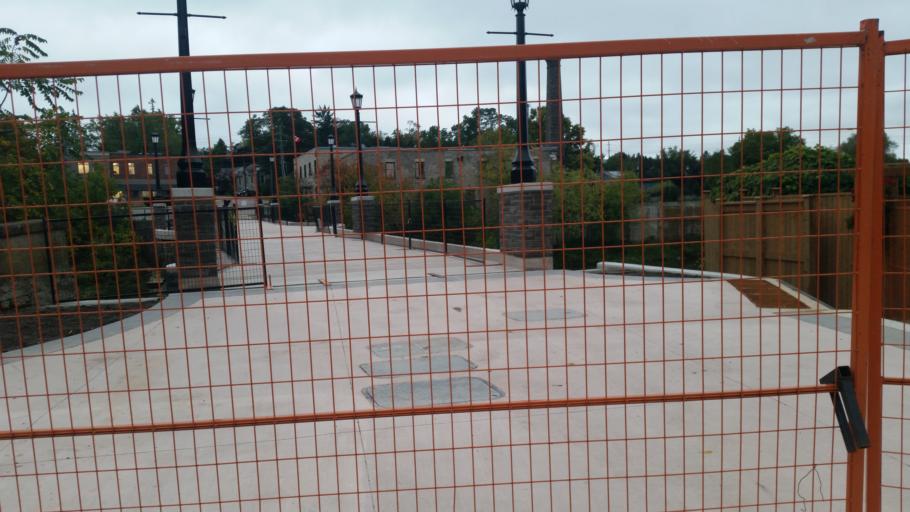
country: CA
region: Ontario
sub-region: Wellington County
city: Guelph
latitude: 43.6808
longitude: -80.4305
